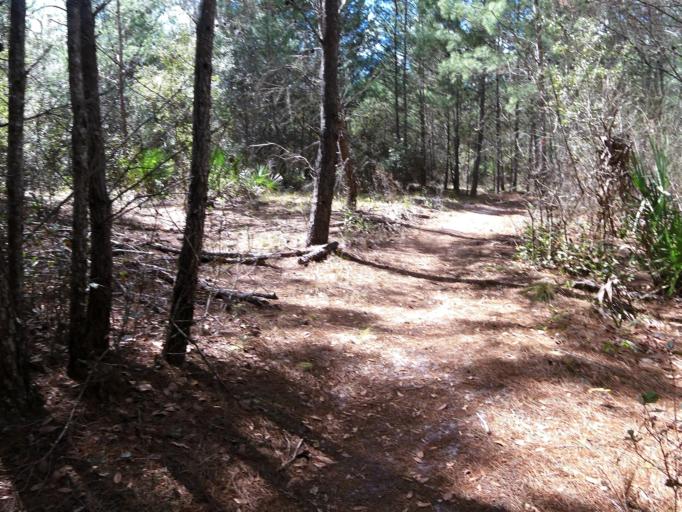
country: US
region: Florida
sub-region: Putnam County
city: Interlachen
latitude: 29.7634
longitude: -81.8567
